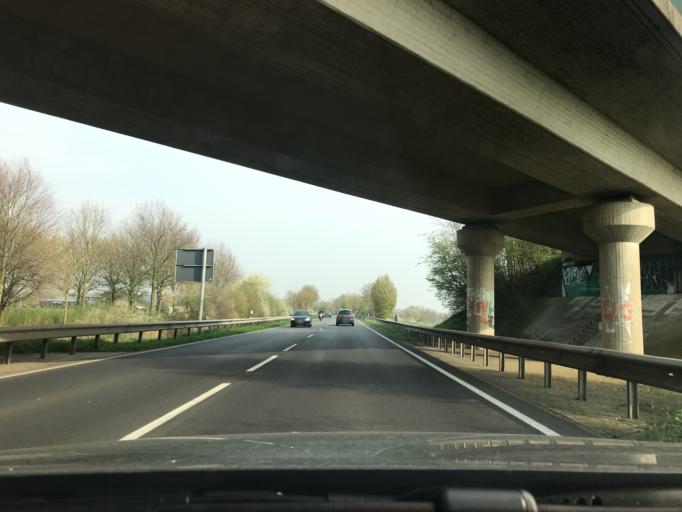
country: DE
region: North Rhine-Westphalia
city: Geldern
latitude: 51.4988
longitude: 6.3187
